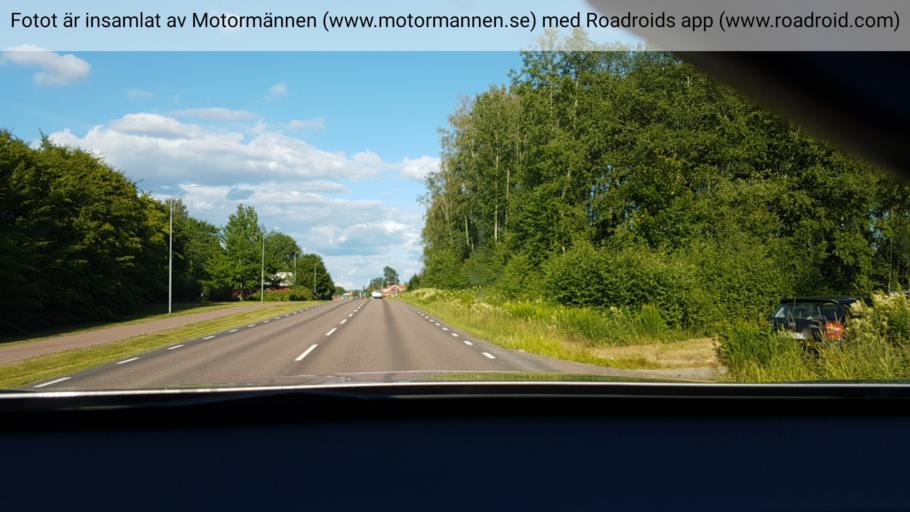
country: SE
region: Vaermland
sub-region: Forshaga Kommun
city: Forshaga
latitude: 59.5198
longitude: 13.4750
